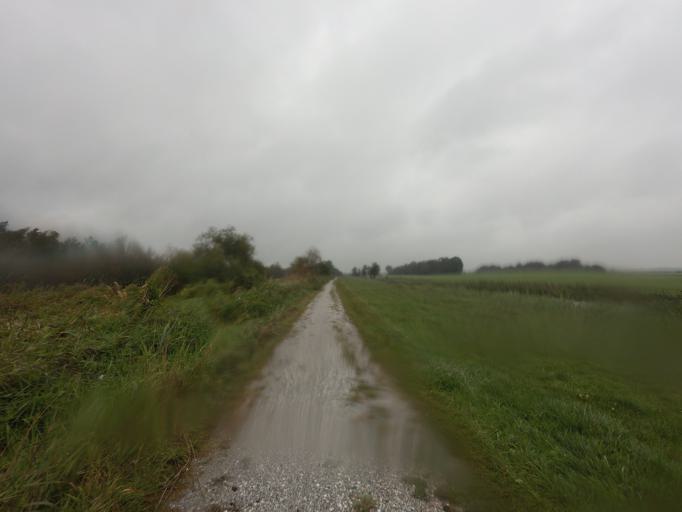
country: NL
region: Friesland
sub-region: Gemeente Smallingerland
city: Oudega
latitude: 53.0971
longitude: 5.9818
